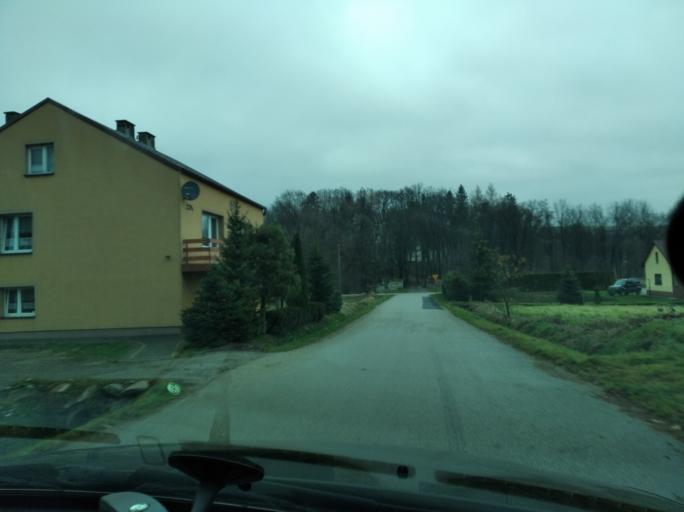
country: PL
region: Subcarpathian Voivodeship
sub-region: Powiat przeworski
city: Jawornik Polski
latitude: 49.9093
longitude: 22.2816
